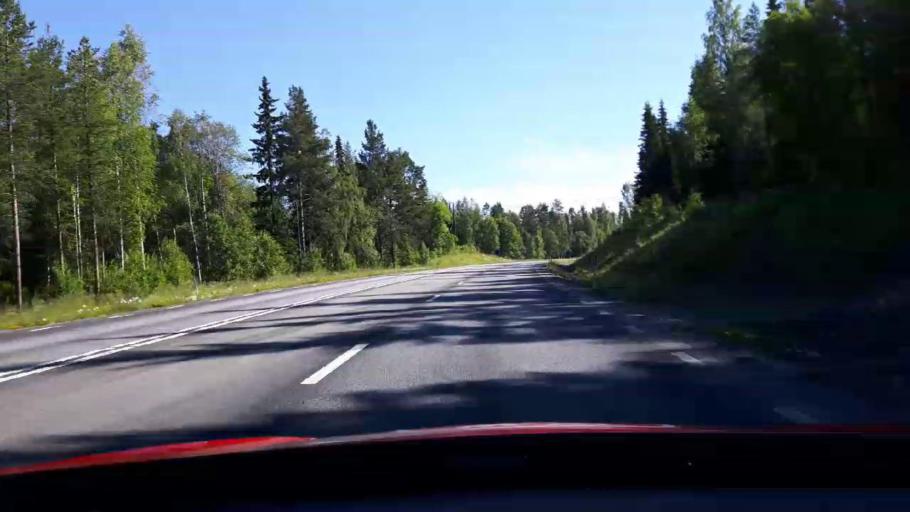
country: SE
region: Jaemtland
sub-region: OEstersunds Kommun
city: Ostersund
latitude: 63.2073
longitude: 14.6851
